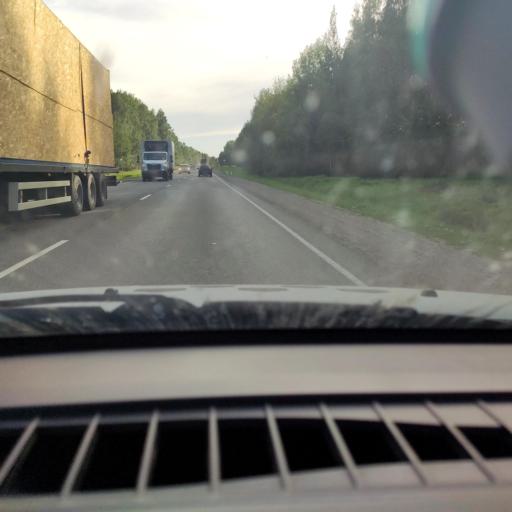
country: RU
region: Kirov
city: Vakhrushi
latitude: 58.6450
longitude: 49.8577
